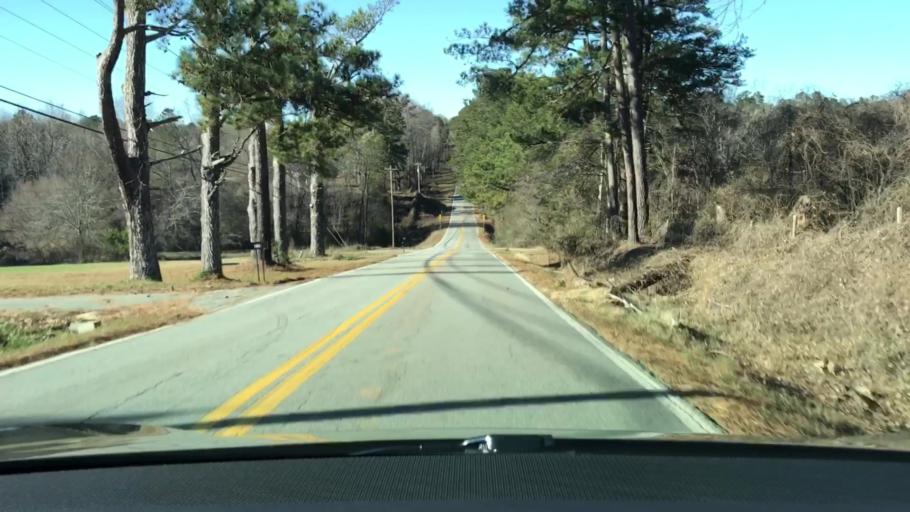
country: US
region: Georgia
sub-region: Barrow County
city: Auburn
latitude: 34.0480
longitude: -83.8462
